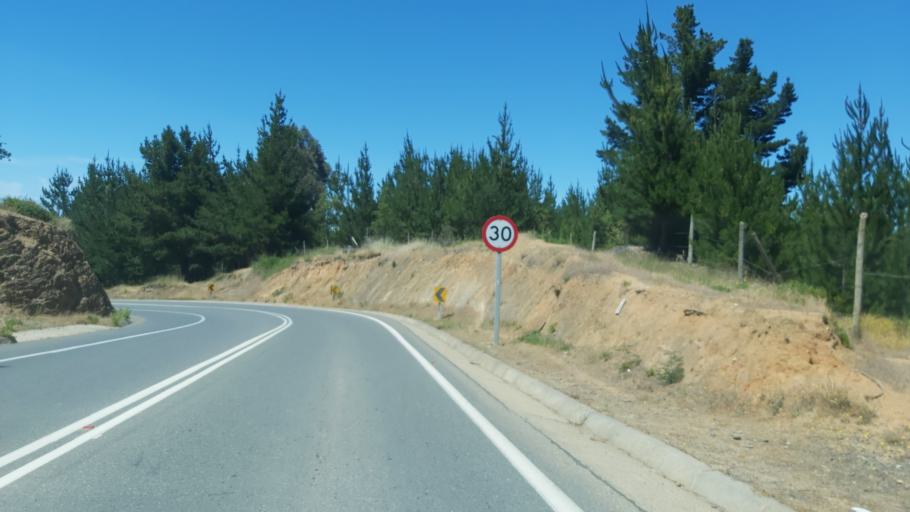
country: CL
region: Maule
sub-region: Provincia de Talca
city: Talca
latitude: -34.9745
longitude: -71.9653
